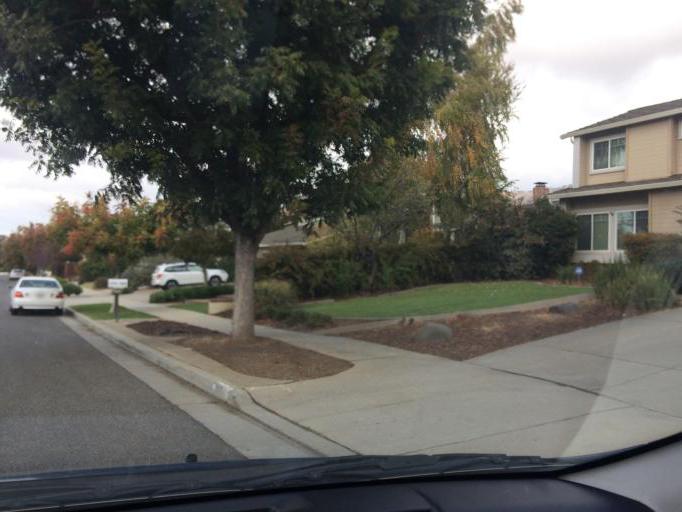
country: US
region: California
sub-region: Santa Clara County
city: Seven Trees
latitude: 37.2916
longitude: -121.7592
